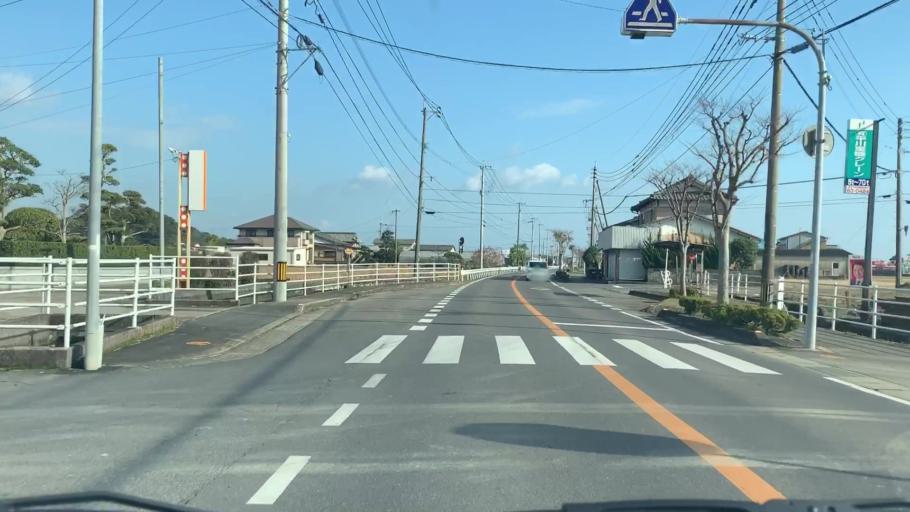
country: JP
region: Saga Prefecture
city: Kashima
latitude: 33.1235
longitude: 130.0790
